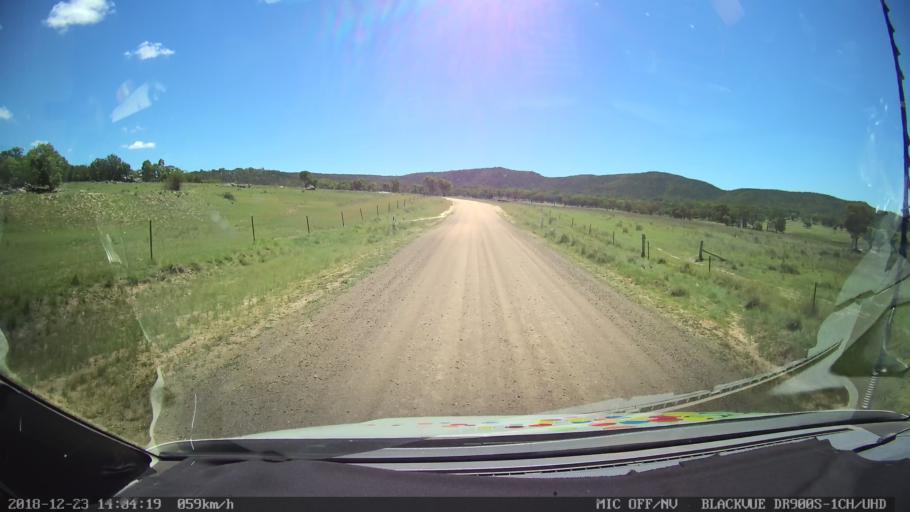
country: AU
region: New South Wales
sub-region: Tamworth Municipality
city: Manilla
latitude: -30.6222
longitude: 151.0917
